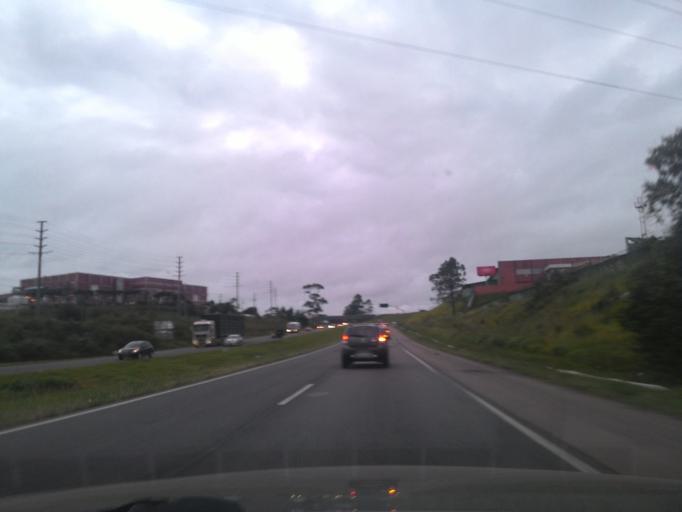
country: BR
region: Parana
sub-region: Sao Jose Dos Pinhais
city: Sao Jose dos Pinhais
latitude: -25.5441
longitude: -49.3147
